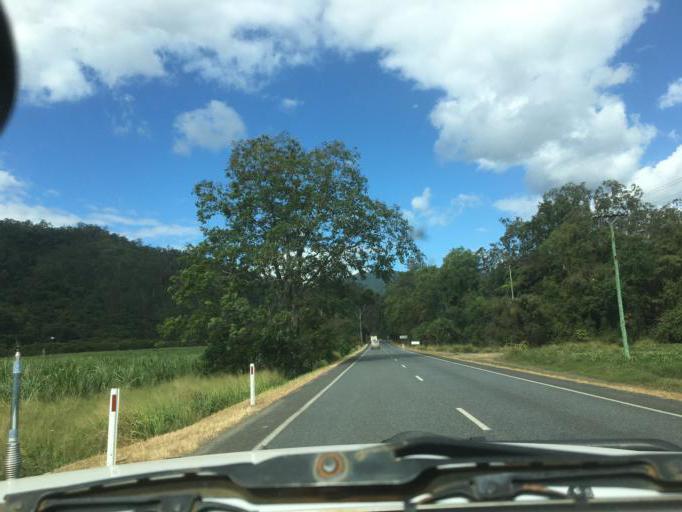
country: AU
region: Queensland
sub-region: Cairns
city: Woree
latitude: -17.1372
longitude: 145.7292
